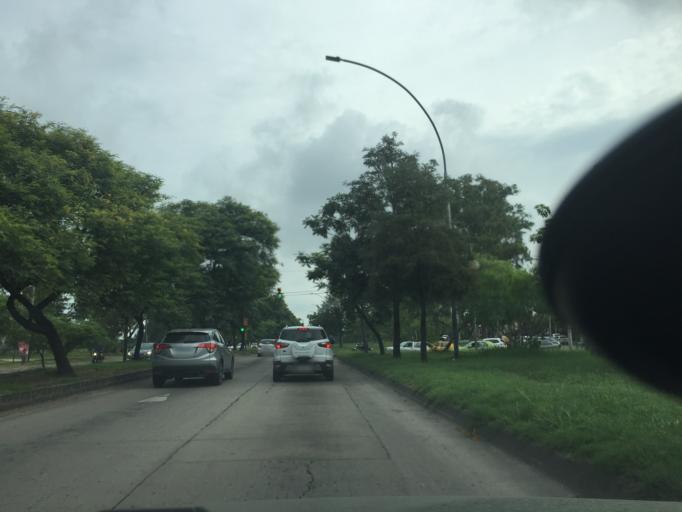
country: AR
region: Cordoba
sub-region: Departamento de Capital
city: Cordoba
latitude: -31.4378
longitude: -64.1960
